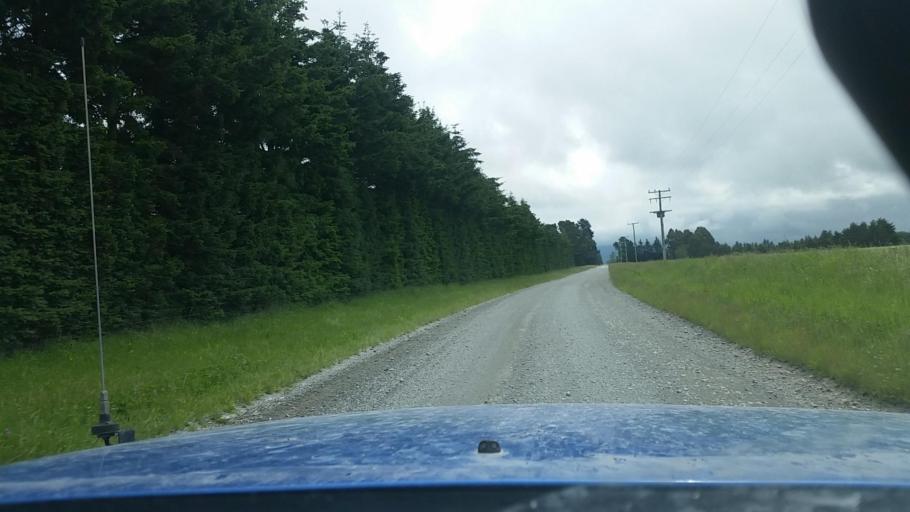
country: NZ
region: Canterbury
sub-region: Ashburton District
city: Methven
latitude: -43.7534
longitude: 171.4779
